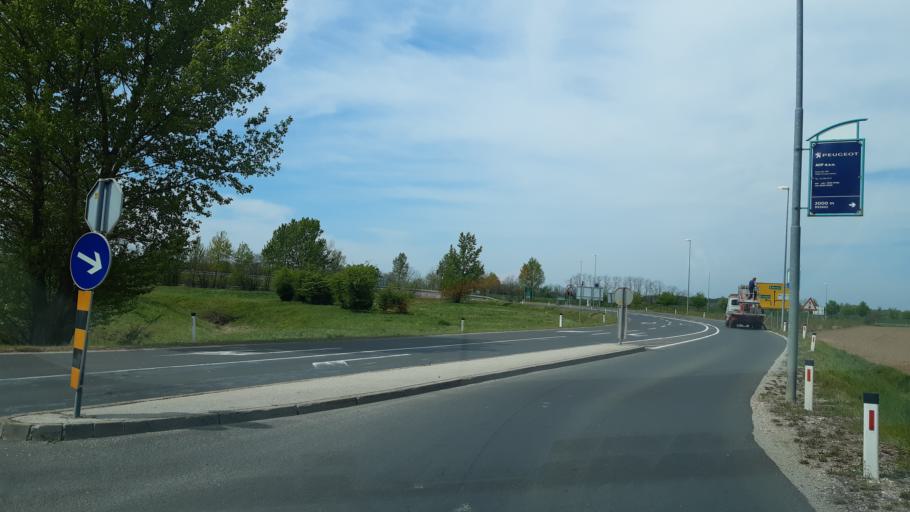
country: SI
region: Murska Sobota
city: Krog
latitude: 46.6358
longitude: 16.1593
